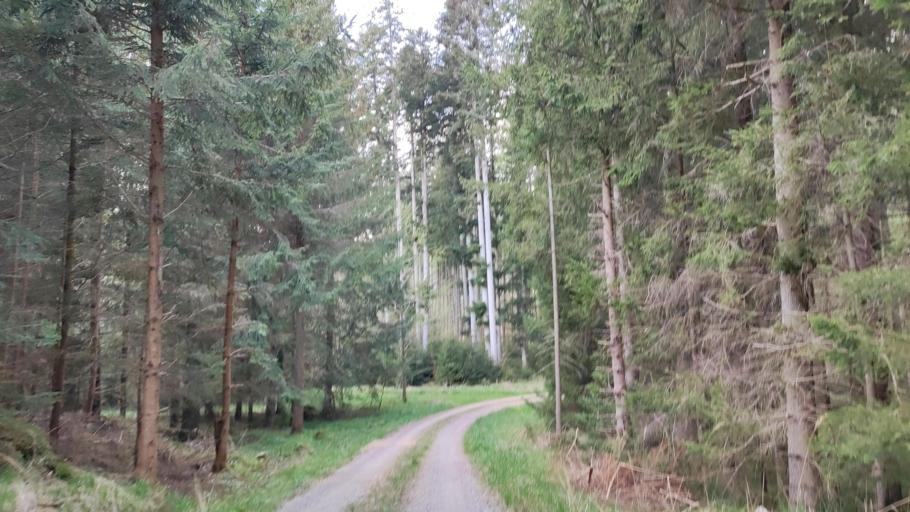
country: DE
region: Bavaria
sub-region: Swabia
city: Zusmarshausen
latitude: 48.3918
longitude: 10.5541
